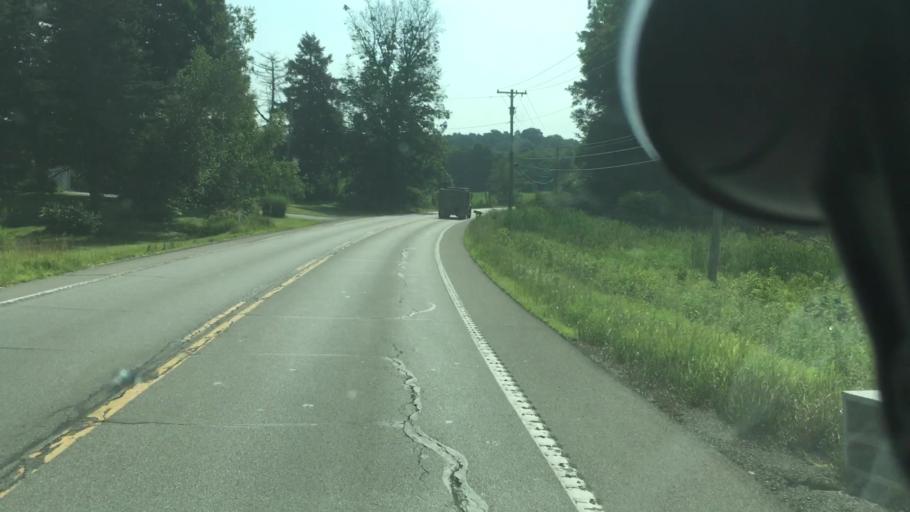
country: US
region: Pennsylvania
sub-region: Lawrence County
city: New Castle
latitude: 41.0137
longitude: -80.2469
